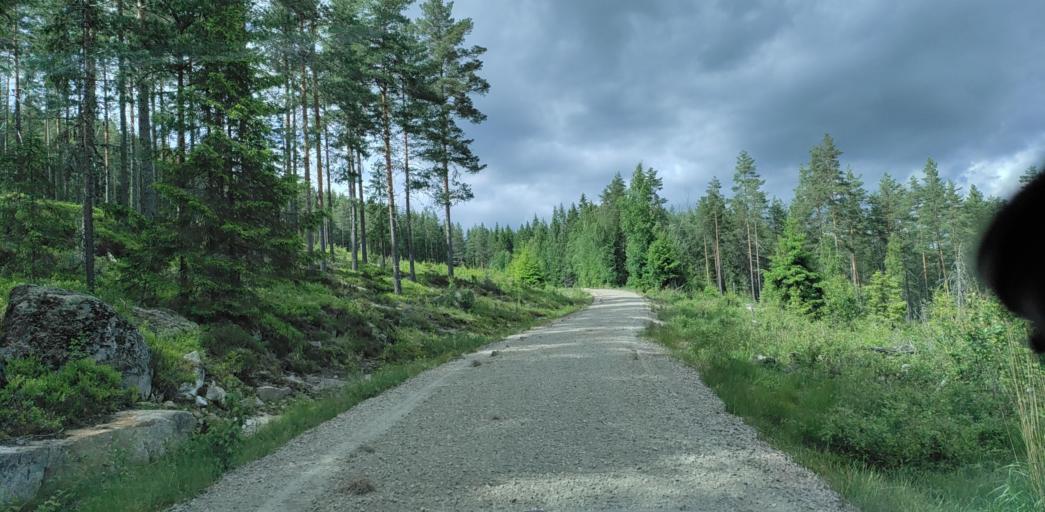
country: SE
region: Vaermland
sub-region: Munkfors Kommun
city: Munkfors
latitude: 59.9658
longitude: 13.4140
